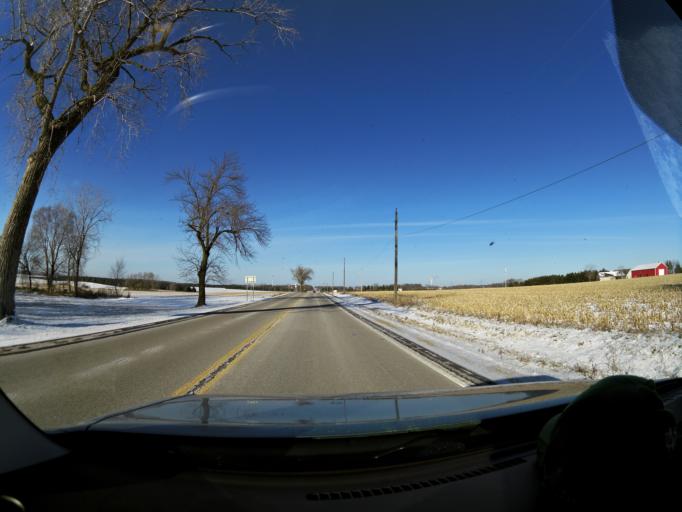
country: US
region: Minnesota
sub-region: Washington County
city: Afton
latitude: 44.8636
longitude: -92.8625
